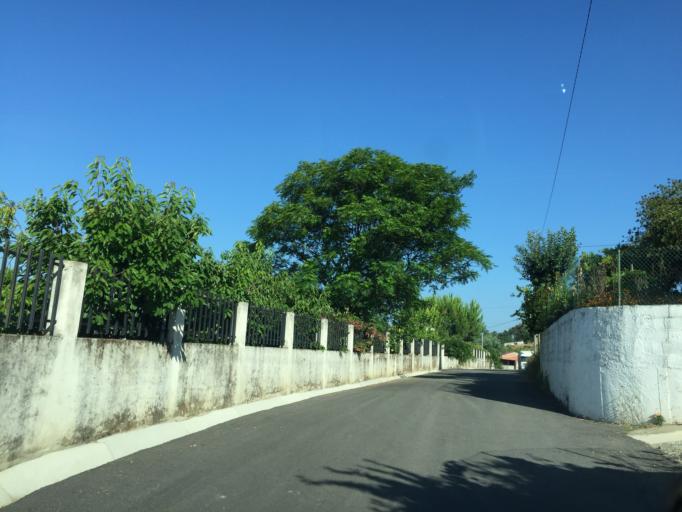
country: PT
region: Santarem
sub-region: Abrantes
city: Alferrarede
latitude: 39.5210
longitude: -8.1370
